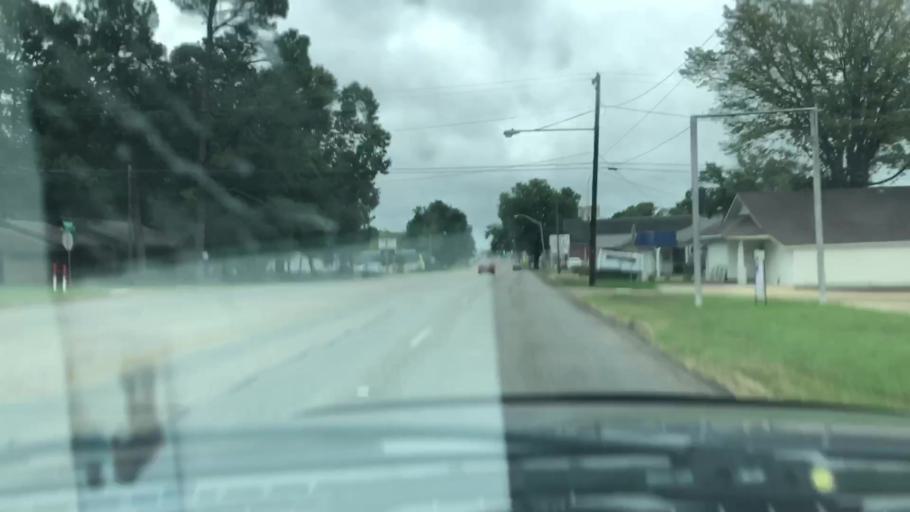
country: US
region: Arkansas
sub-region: Miller County
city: Texarkana
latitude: 33.4436
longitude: -94.0532
